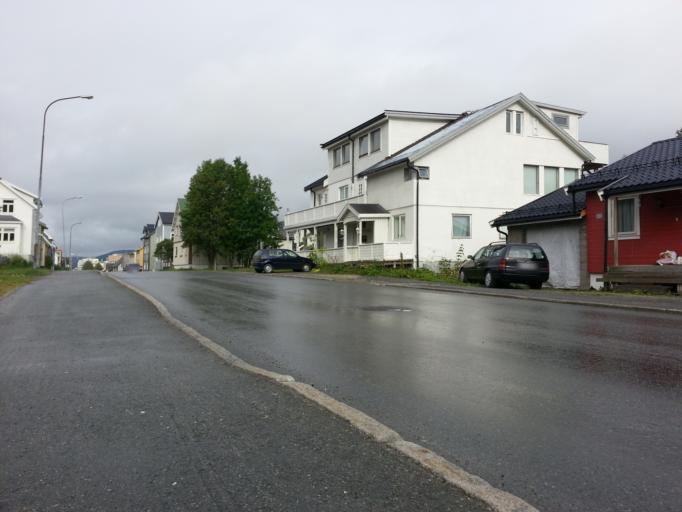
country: NO
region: Troms
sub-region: Tromso
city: Tromso
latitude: 69.6405
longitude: 18.9368
